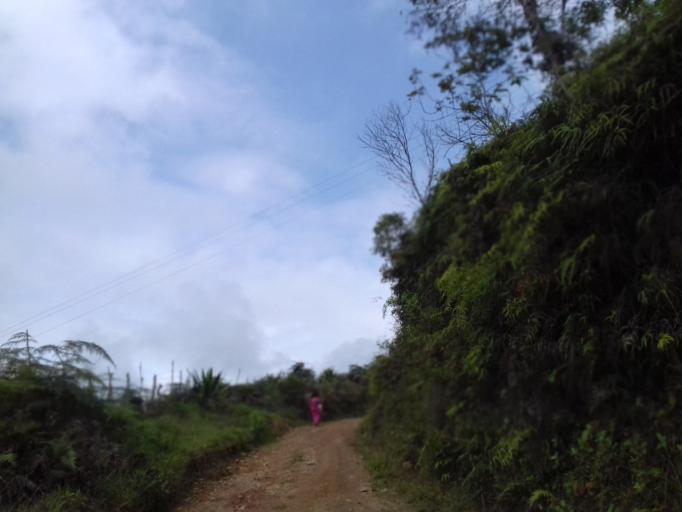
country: CO
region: Tolima
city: Libano
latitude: 4.9350
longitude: -75.0485
